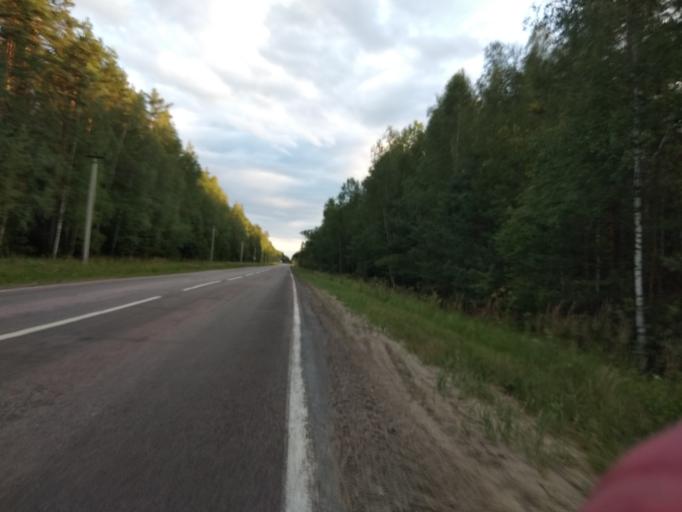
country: RU
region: Moskovskaya
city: Misheronskiy
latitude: 55.6238
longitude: 39.7327
